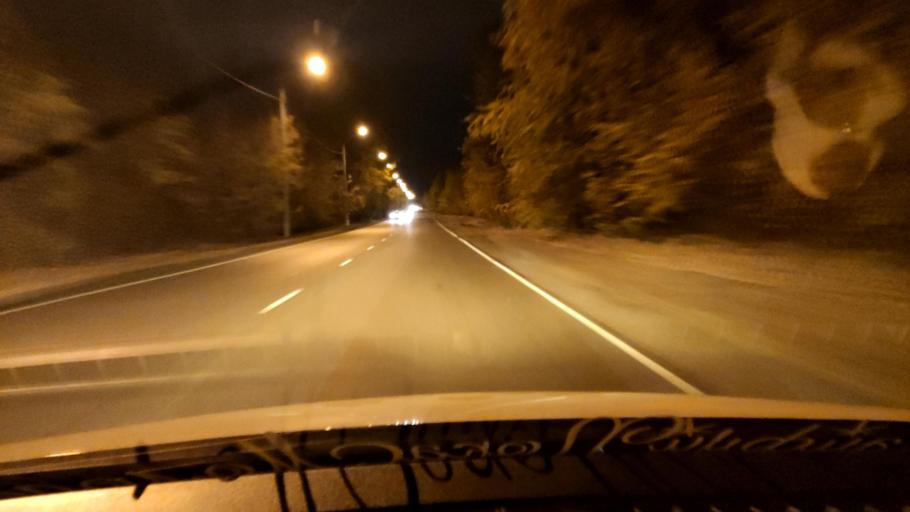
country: RU
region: Voronezj
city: Maslovka
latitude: 51.5901
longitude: 39.1745
